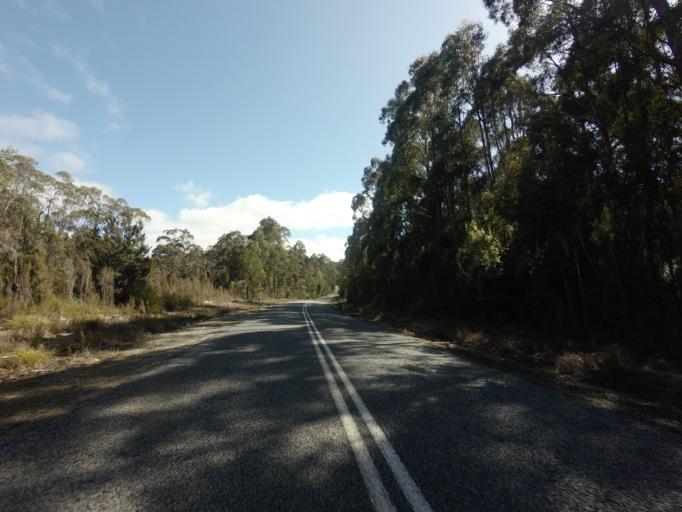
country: AU
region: Tasmania
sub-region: Huon Valley
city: Geeveston
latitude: -42.7668
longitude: 146.3972
